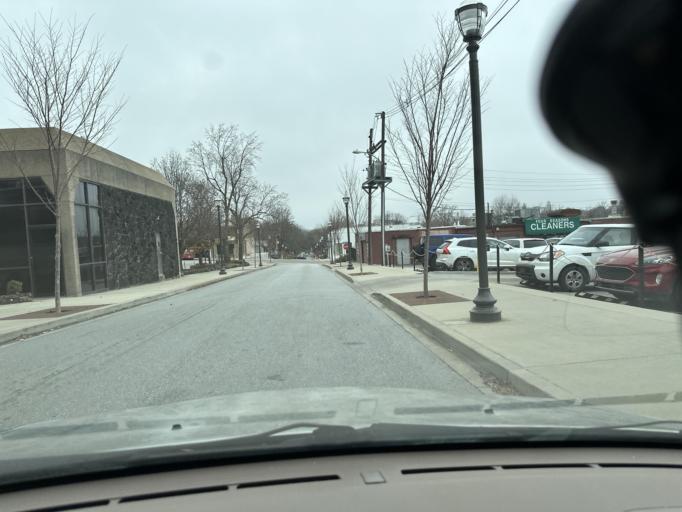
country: US
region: Arkansas
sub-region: Washington County
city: Fayetteville
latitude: 36.0637
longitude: -94.1597
